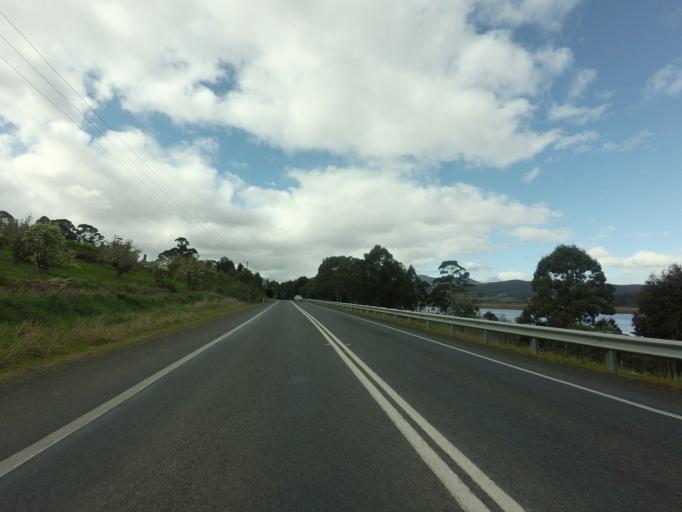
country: AU
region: Tasmania
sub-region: Huon Valley
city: Franklin
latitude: -43.1114
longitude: 146.9971
